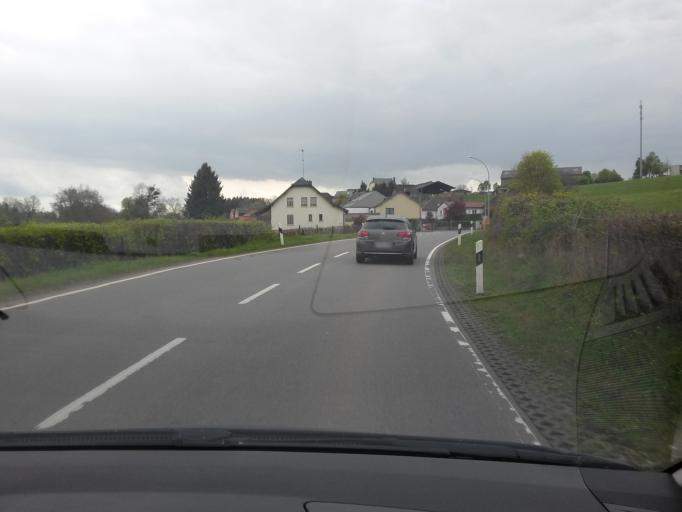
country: LU
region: Luxembourg
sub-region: Canton de Capellen
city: Garnich
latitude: 49.6050
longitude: 5.9481
